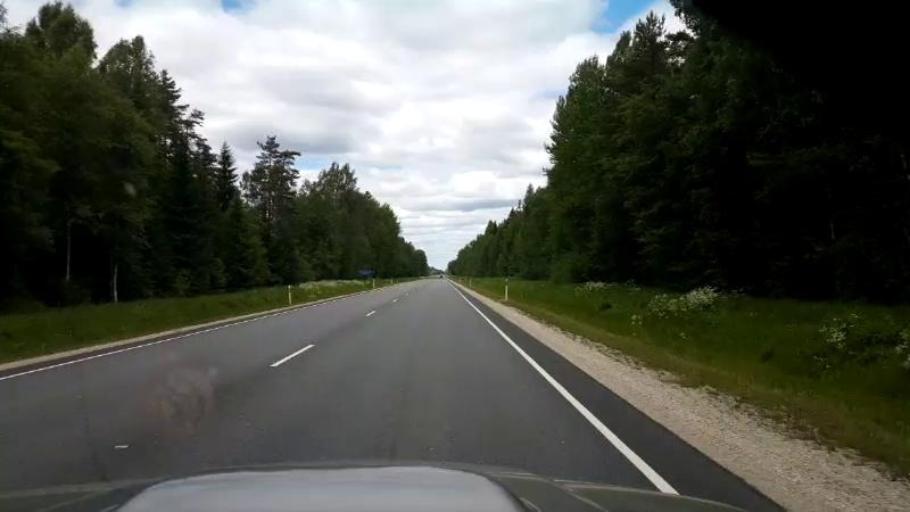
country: EE
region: Raplamaa
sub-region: Maerjamaa vald
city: Marjamaa
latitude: 58.7935
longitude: 24.4129
